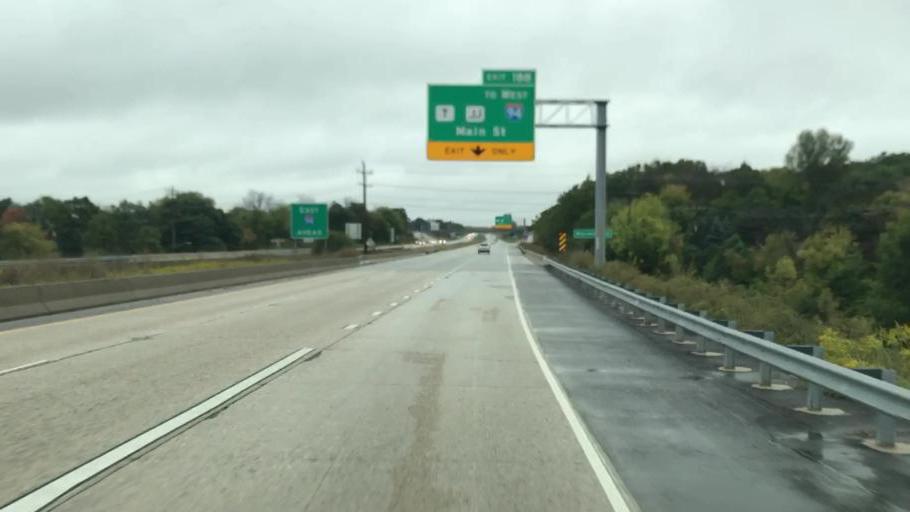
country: US
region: Wisconsin
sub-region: Waukesha County
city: Pewaukee
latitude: 43.0794
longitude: -88.2515
